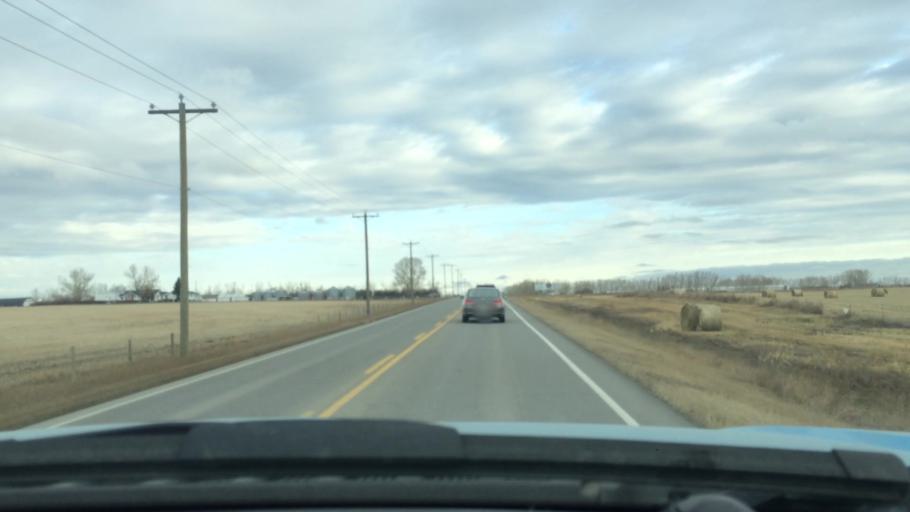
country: CA
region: Alberta
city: Airdrie
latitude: 51.2245
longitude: -114.0249
